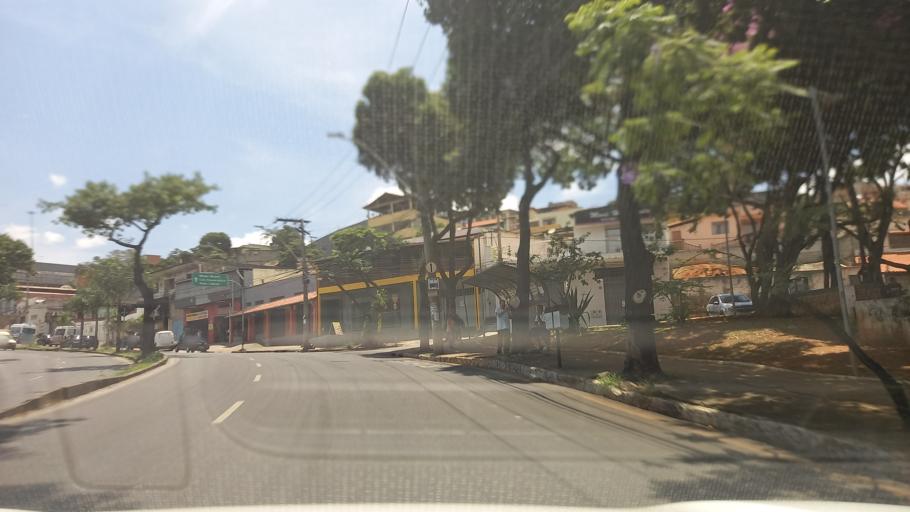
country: BR
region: Minas Gerais
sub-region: Belo Horizonte
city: Belo Horizonte
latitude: -19.9143
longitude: -43.9963
